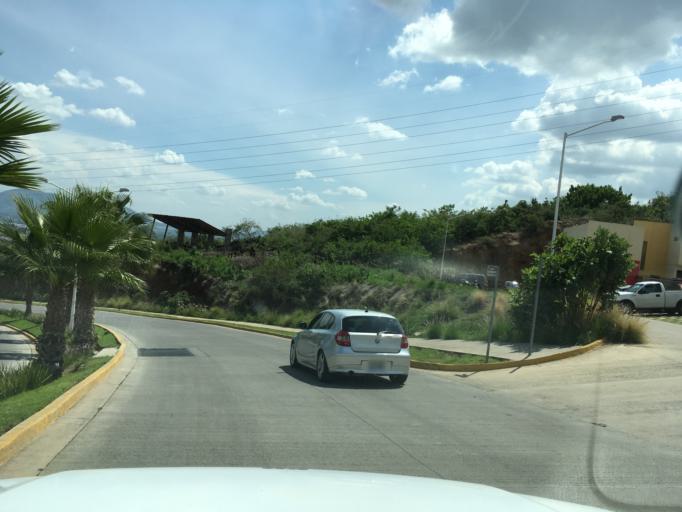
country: MX
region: Jalisco
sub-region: Tlajomulco de Zuniga
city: Altus Bosques
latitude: 20.5899
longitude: -103.3608
